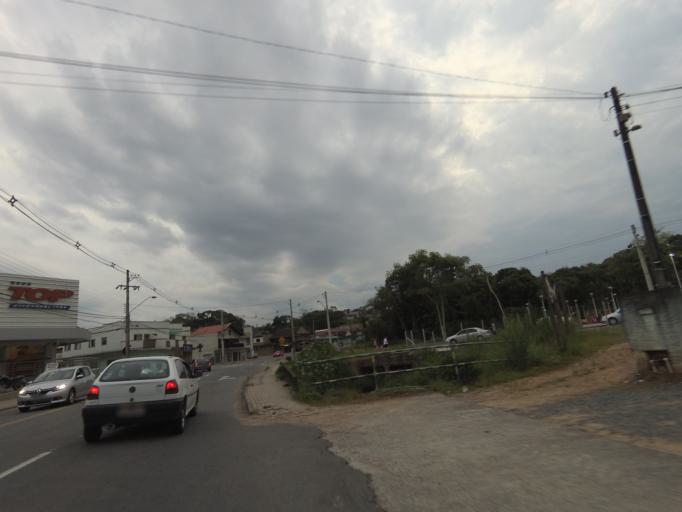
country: BR
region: Santa Catarina
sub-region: Blumenau
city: Blumenau
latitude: -26.8748
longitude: -49.0542
